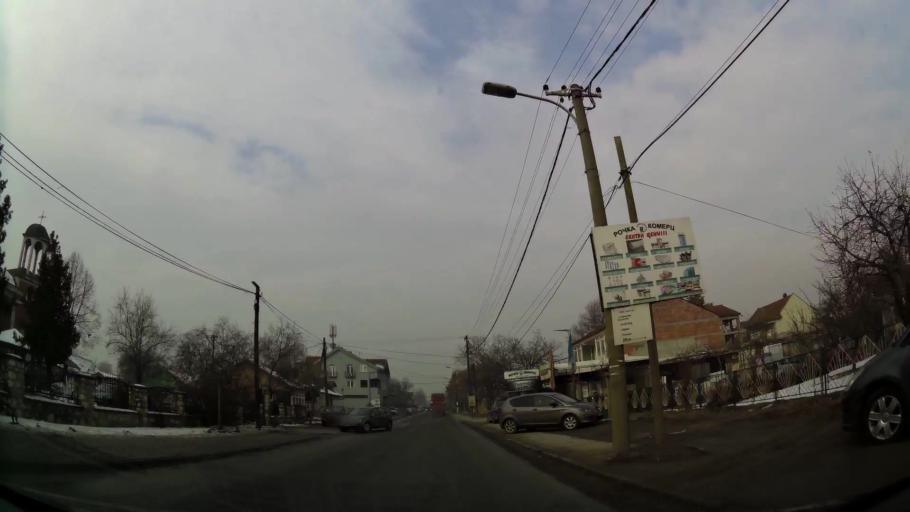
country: MK
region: Kisela Voda
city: Kisela Voda
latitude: 41.9948
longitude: 21.5034
